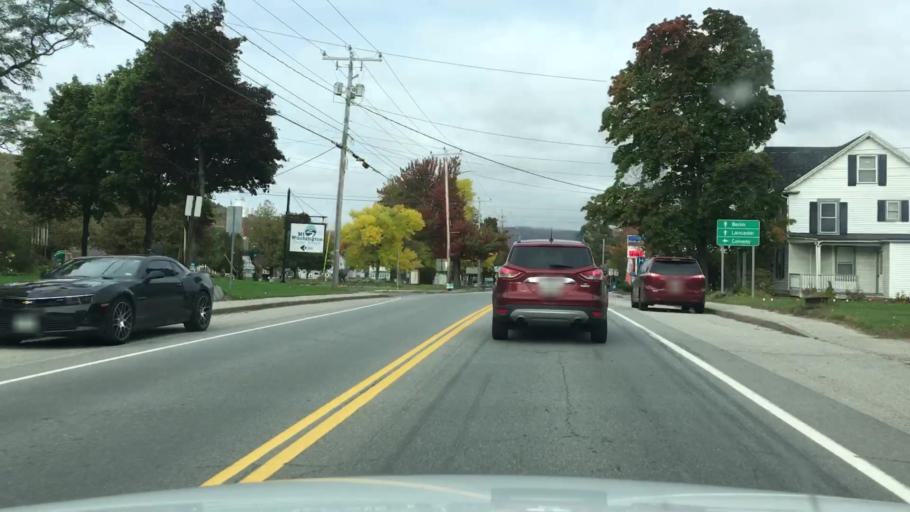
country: US
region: New Hampshire
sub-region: Coos County
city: Gorham
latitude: 44.3878
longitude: -71.1720
